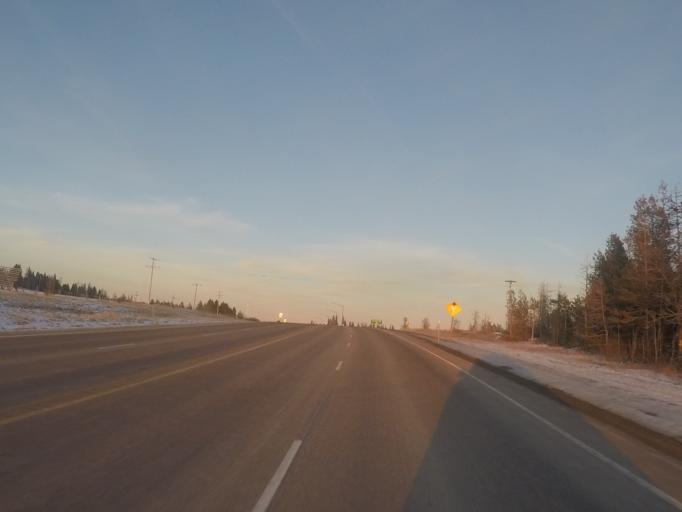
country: US
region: Montana
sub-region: Lewis and Clark County
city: Helena West Side
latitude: 46.5601
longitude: -112.3127
